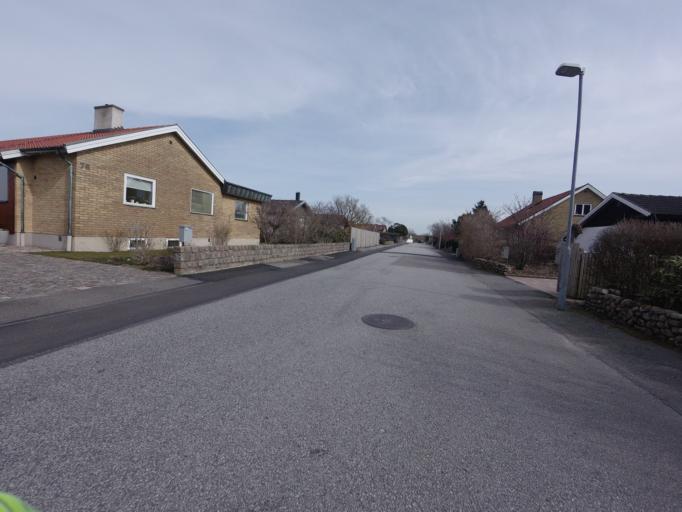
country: SE
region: Skane
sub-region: Hoganas Kommun
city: Hoganas
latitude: 56.1506
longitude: 12.5762
